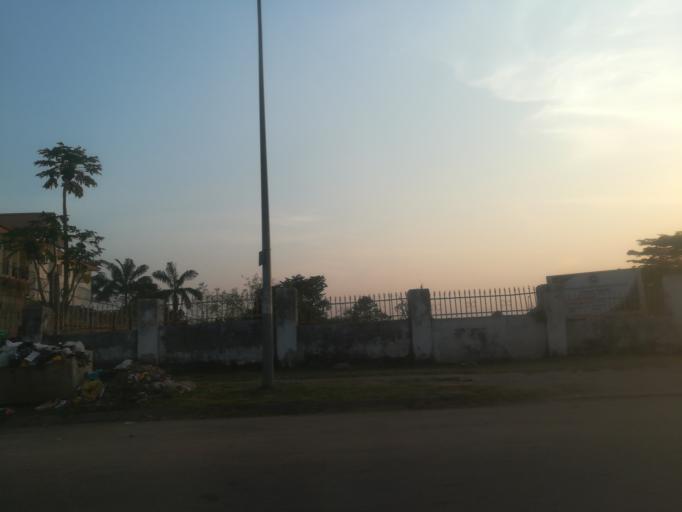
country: NG
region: Abuja Federal Capital Territory
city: Abuja
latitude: 9.0624
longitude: 7.4397
